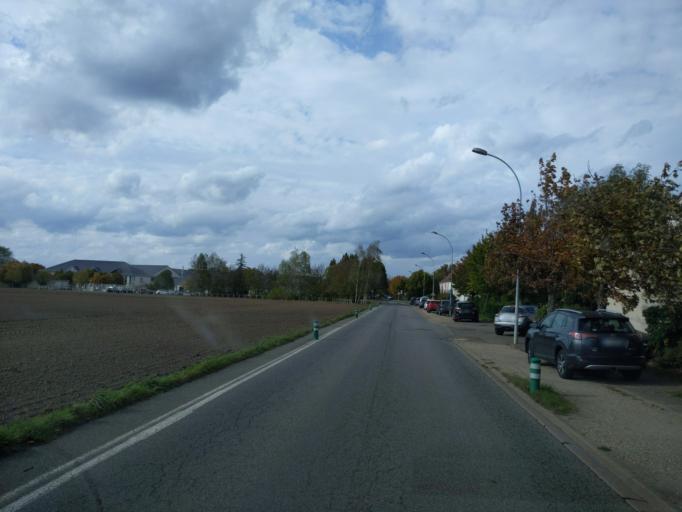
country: FR
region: Ile-de-France
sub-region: Departement des Yvelines
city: Rambouillet
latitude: 48.6467
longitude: 1.8514
